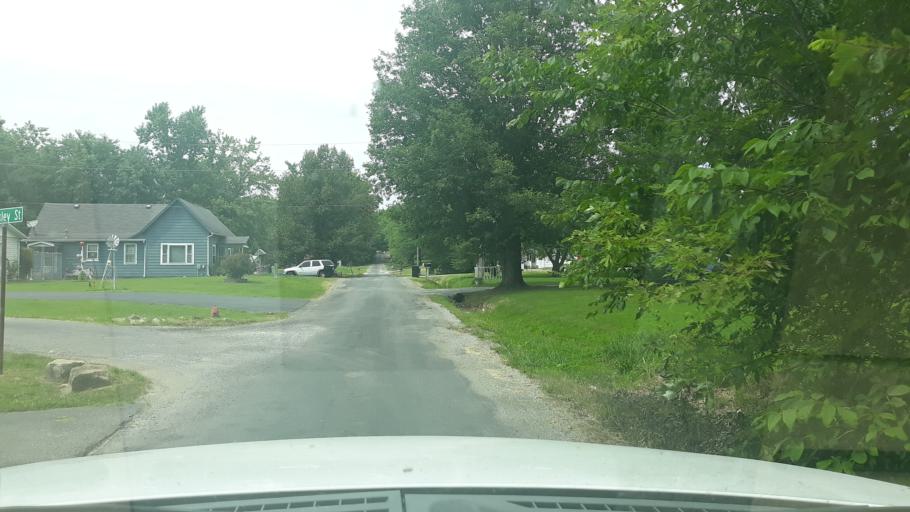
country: US
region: Illinois
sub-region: Saline County
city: Harrisburg
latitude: 37.8450
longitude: -88.6099
